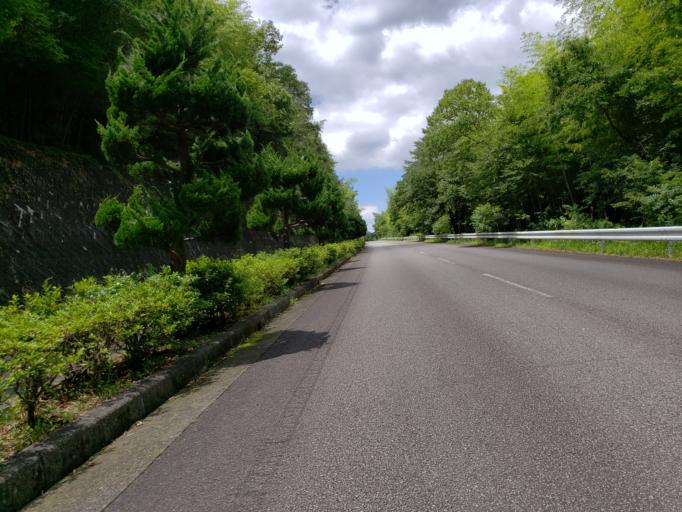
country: JP
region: Hyogo
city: Himeji
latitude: 34.8602
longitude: 134.7564
